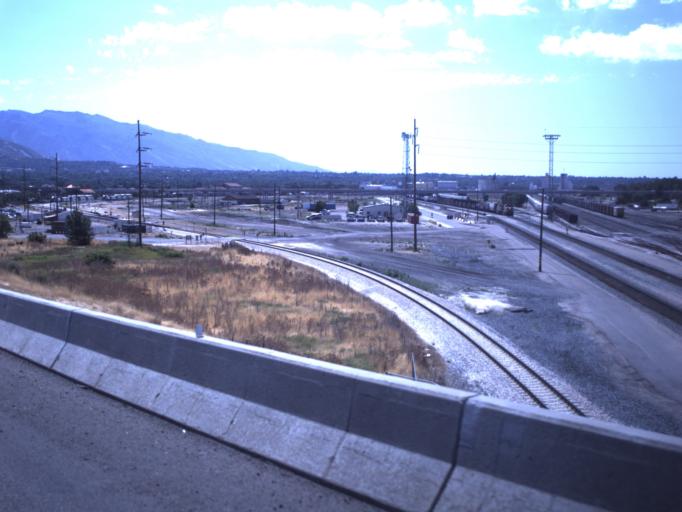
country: US
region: Utah
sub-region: Weber County
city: Ogden
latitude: 41.2309
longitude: -111.9865
